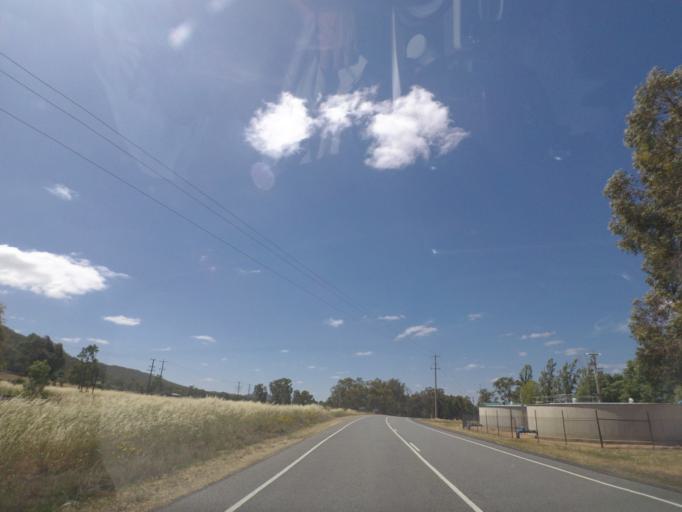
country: AU
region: Victoria
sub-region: Wangaratta
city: Wangaratta
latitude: -36.4514
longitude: 146.2380
